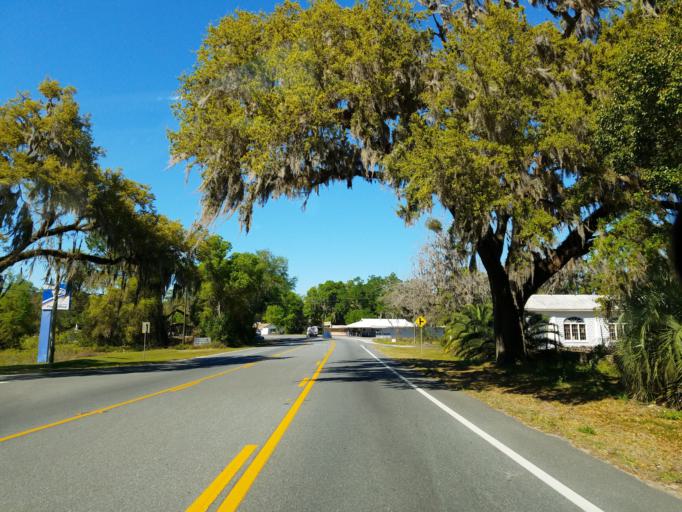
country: US
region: Florida
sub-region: Marion County
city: Belleview
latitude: 29.0099
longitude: -82.0413
